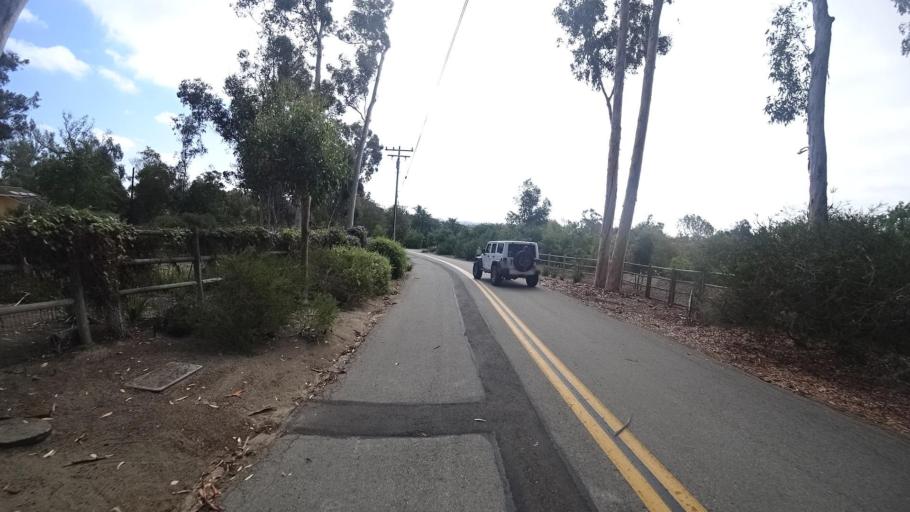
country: US
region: California
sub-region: San Diego County
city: Rancho Santa Fe
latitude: 33.0109
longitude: -117.2082
